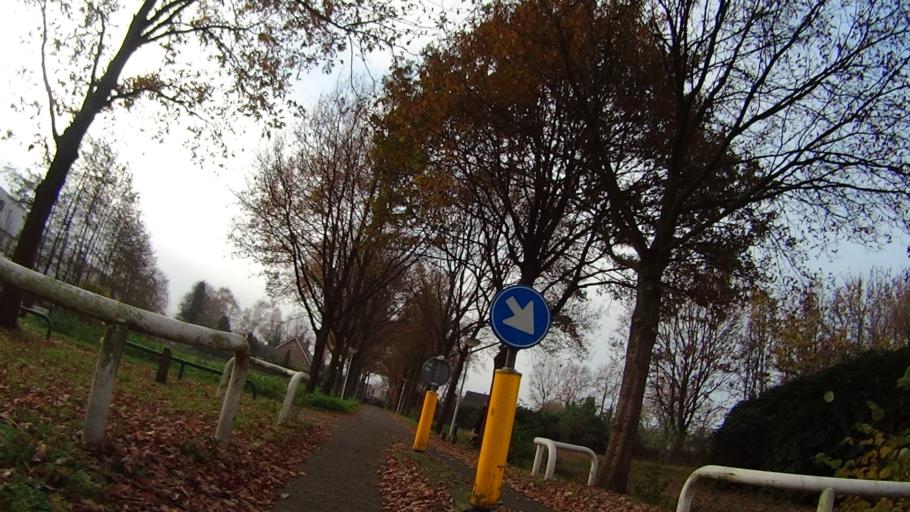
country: NL
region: Utrecht
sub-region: Gemeente Amersfoort
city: Hoogland
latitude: 52.1767
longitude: 5.3940
